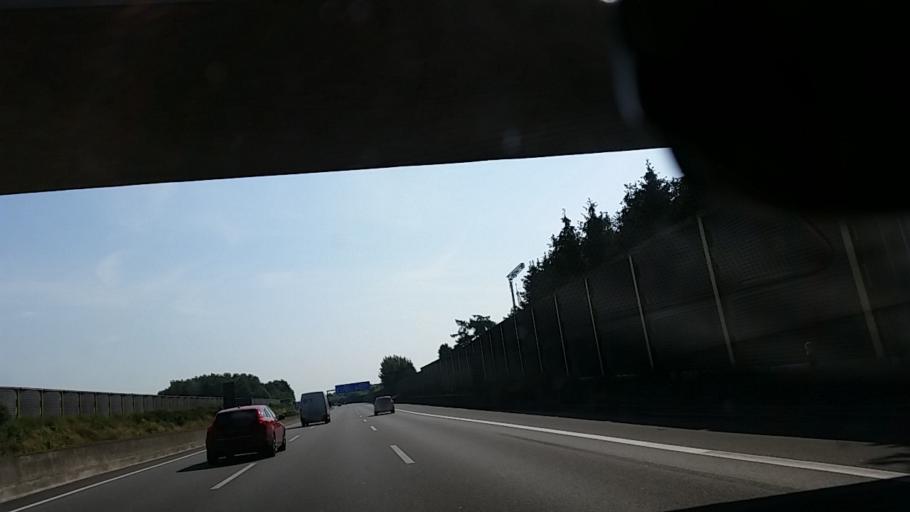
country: DE
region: Lower Saxony
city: Wallenhorst
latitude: 52.3347
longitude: 8.0017
